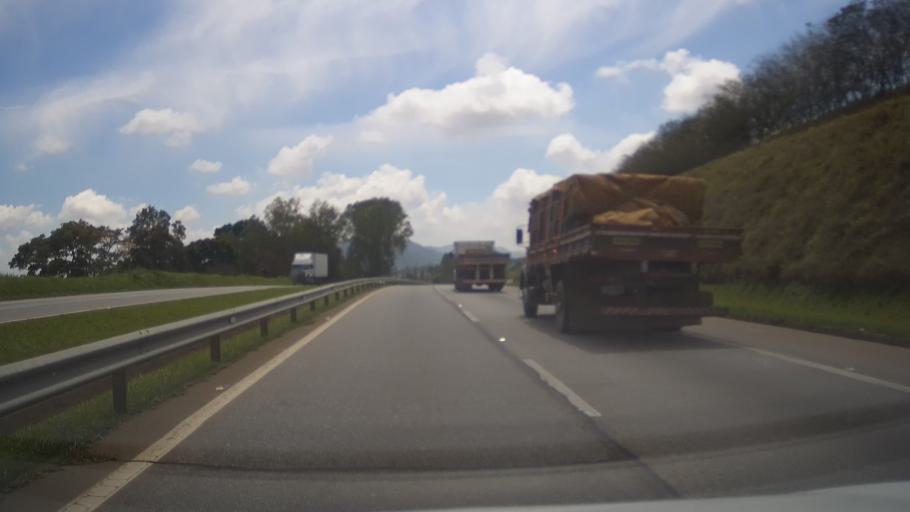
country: BR
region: Minas Gerais
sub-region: Santa Rita Do Sapucai
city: Santa Rita do Sapucai
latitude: -22.0997
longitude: -45.7204
